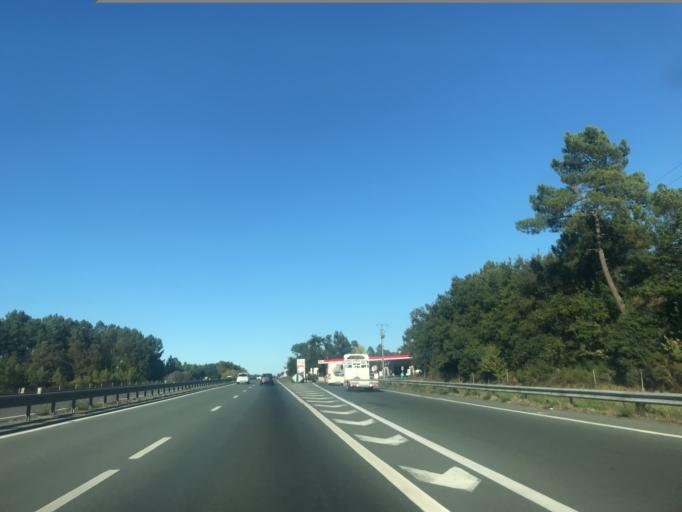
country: FR
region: Aquitaine
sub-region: Departement de la Gironde
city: Laruscade
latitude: 45.1683
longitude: -0.3372
